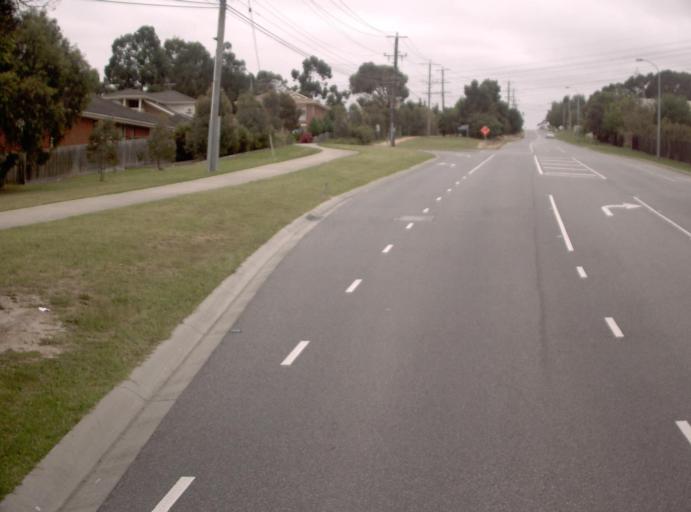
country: AU
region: Victoria
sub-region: Casey
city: Endeavour Hills
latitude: -37.9728
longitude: 145.2798
